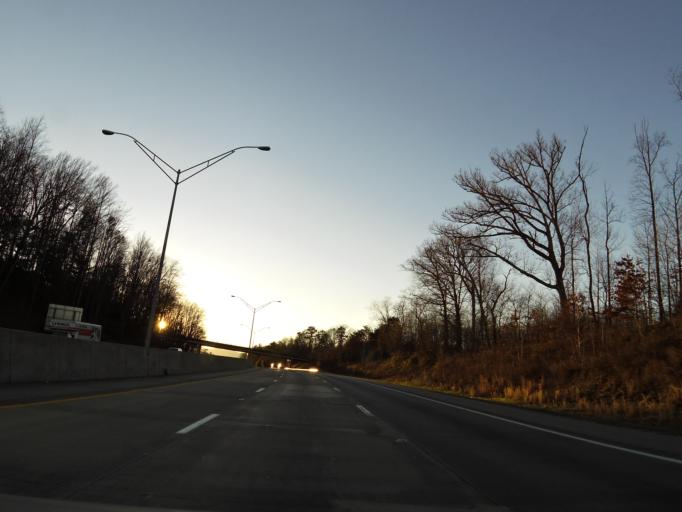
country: US
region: North Carolina
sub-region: Buncombe County
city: Bent Creek
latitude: 35.5595
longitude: -82.6459
